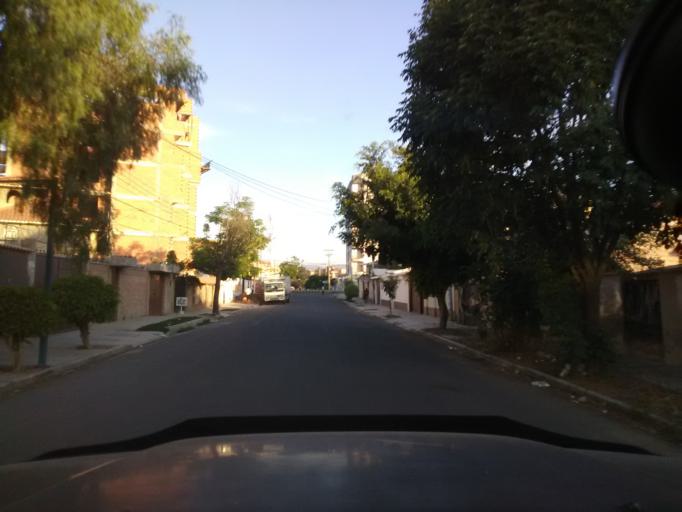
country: BO
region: Cochabamba
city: Cochabamba
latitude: -17.3777
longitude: -66.1700
